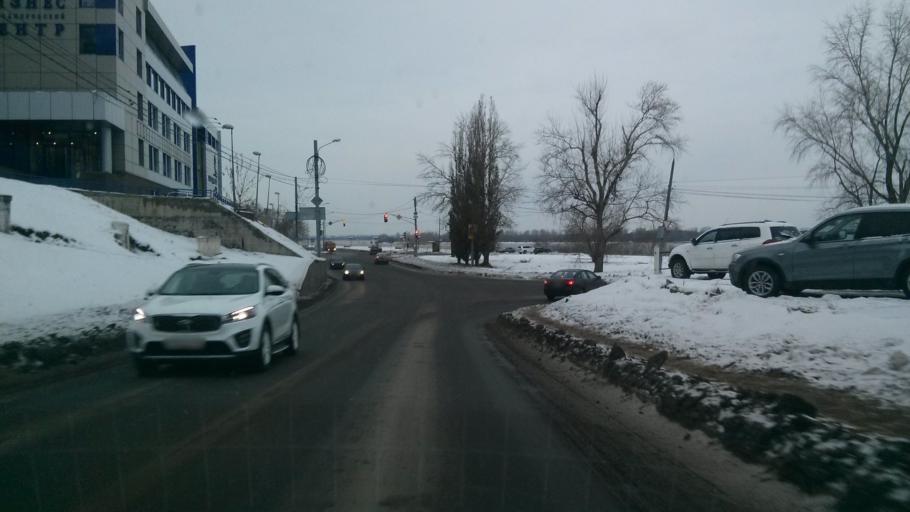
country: RU
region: Nizjnij Novgorod
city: Nizhniy Novgorod
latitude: 56.3295
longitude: 44.0255
